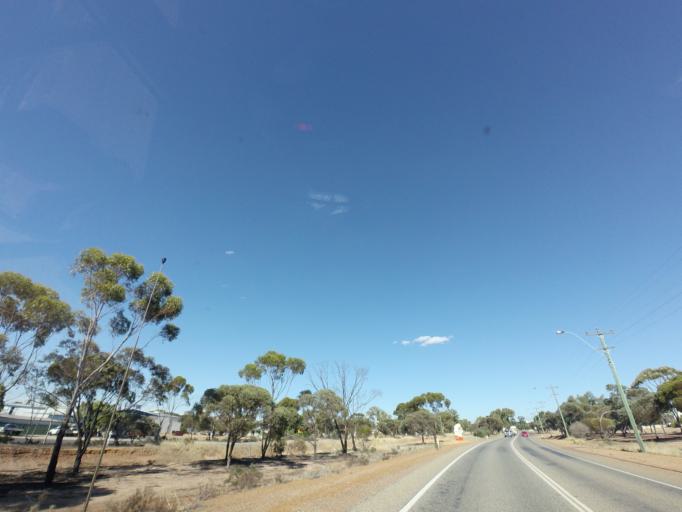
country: AU
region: Western Australia
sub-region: Merredin
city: Merredin
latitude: -31.4817
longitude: 118.2641
